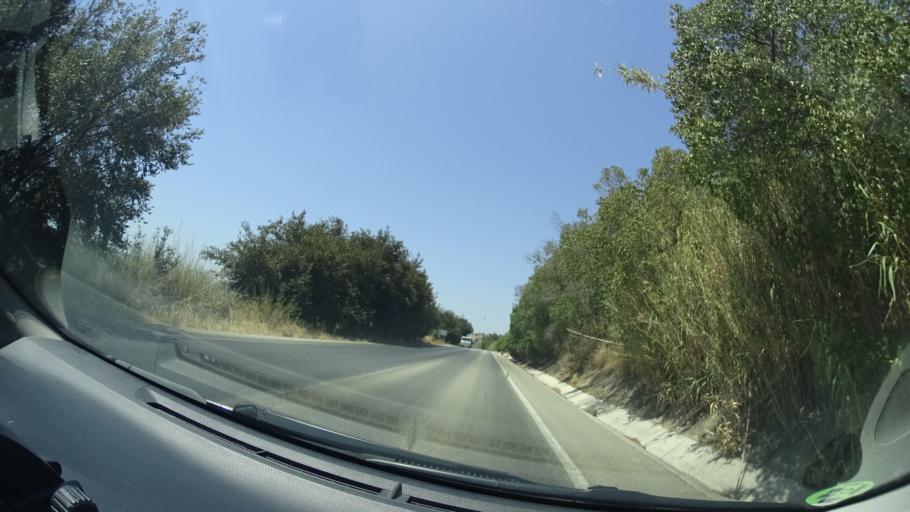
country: ES
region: Andalusia
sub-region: Provincia de Cadiz
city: Jerez de la Frontera
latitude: 36.6565
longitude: -6.0951
